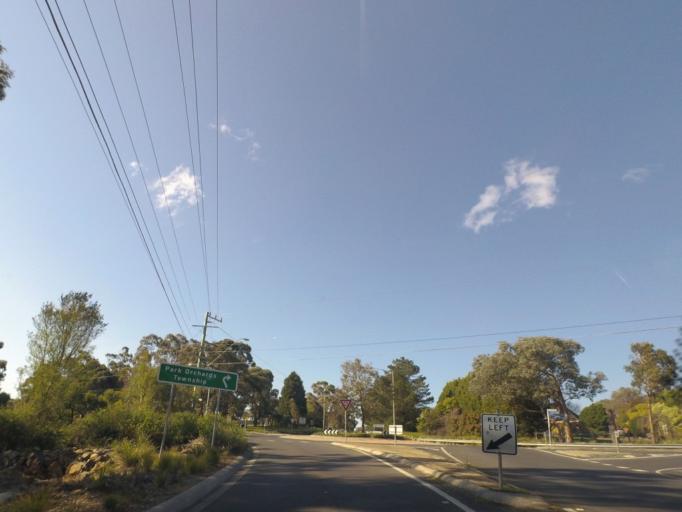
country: AU
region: Victoria
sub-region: Manningham
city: Park Orchards
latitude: -37.7717
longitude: 145.2169
